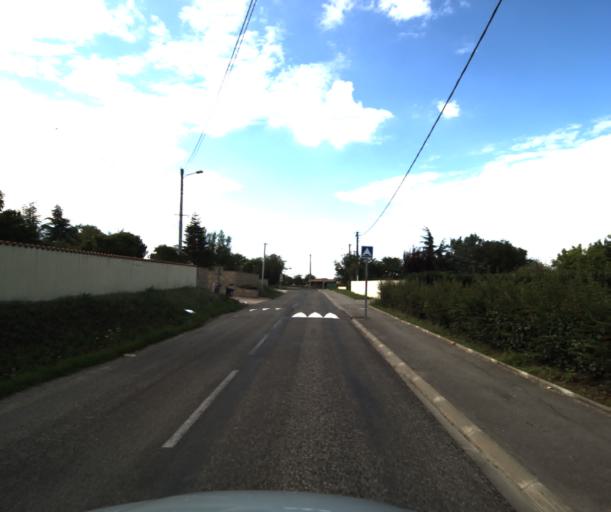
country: FR
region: Midi-Pyrenees
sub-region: Departement de la Haute-Garonne
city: Saubens
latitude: 43.4756
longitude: 1.3524
